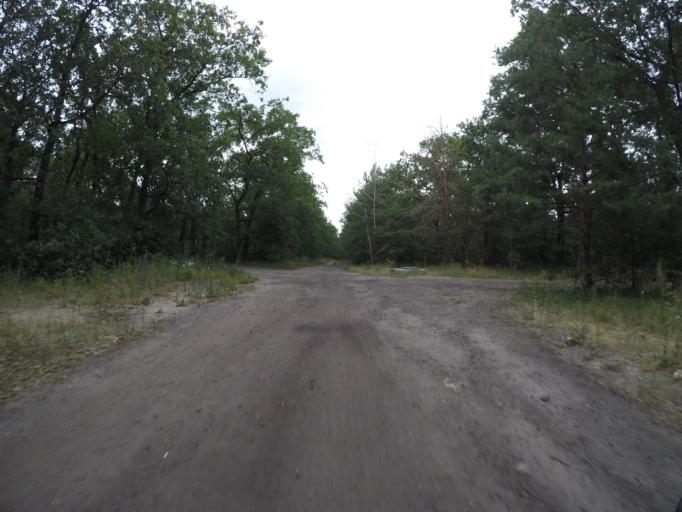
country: DE
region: Berlin
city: Baumschulenweg
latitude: 52.4558
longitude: 13.4956
